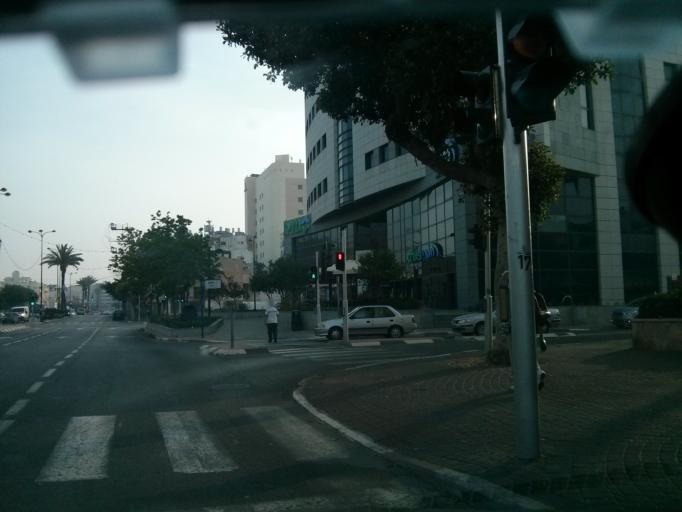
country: IL
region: Central District
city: Netanya
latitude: 32.3250
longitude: 34.8571
